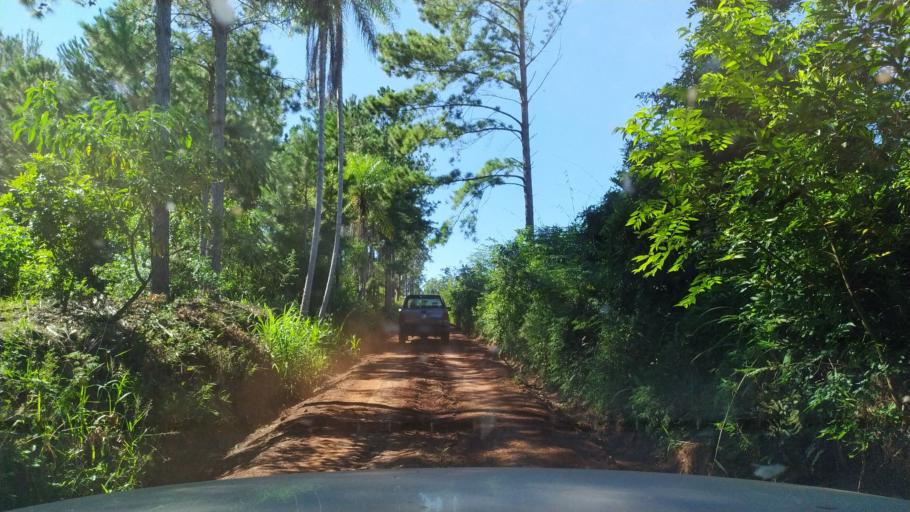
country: AR
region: Misiones
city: Caraguatay
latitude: -26.6688
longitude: -54.6998
